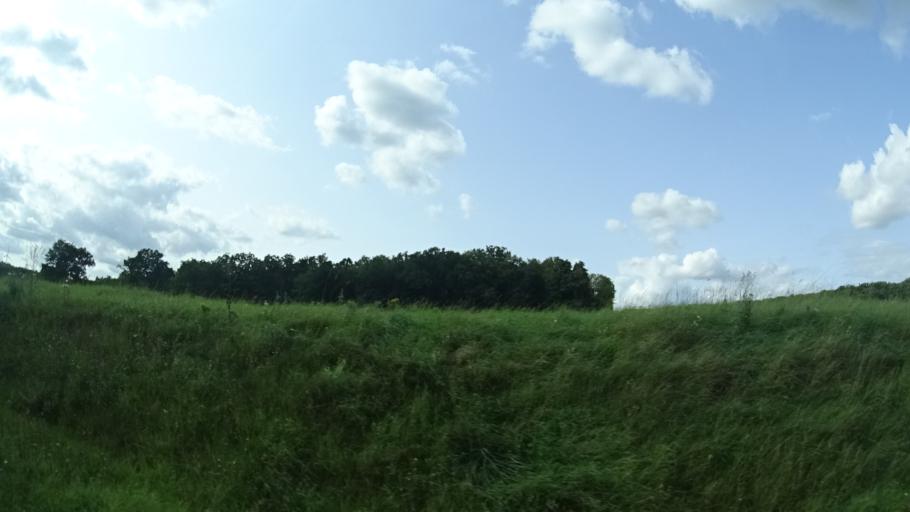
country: DE
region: Bavaria
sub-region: Regierungsbezirk Unterfranken
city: Arnstein
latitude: 49.9237
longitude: 9.9538
